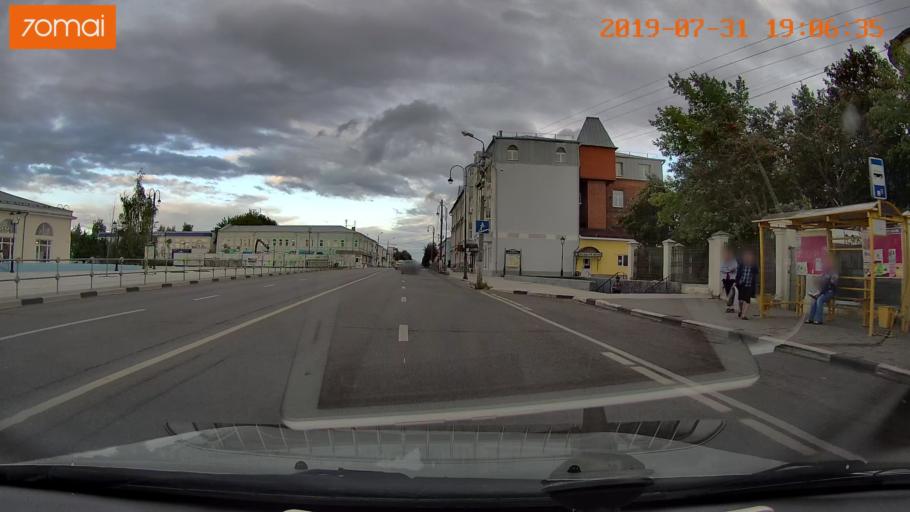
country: RU
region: Moskovskaya
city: Kolomna
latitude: 55.1015
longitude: 38.7547
